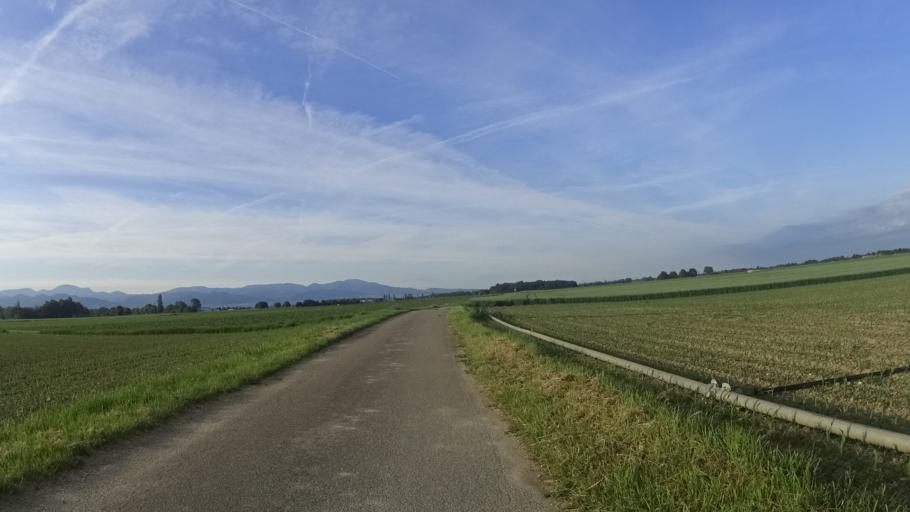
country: DE
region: Baden-Wuerttemberg
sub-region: Freiburg Region
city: Hartheim
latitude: 47.9616
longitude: 7.6440
